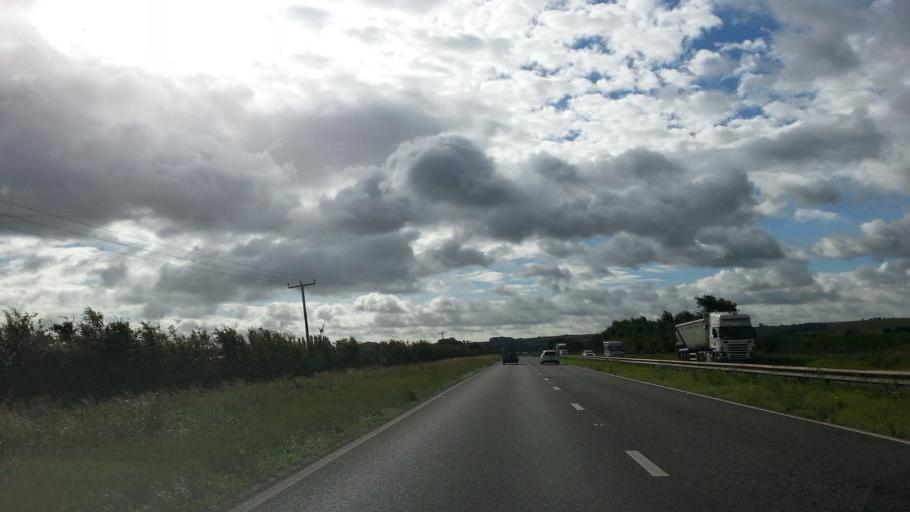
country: GB
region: England
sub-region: Lincolnshire
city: Great Gonerby
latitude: 52.9677
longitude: -0.7035
